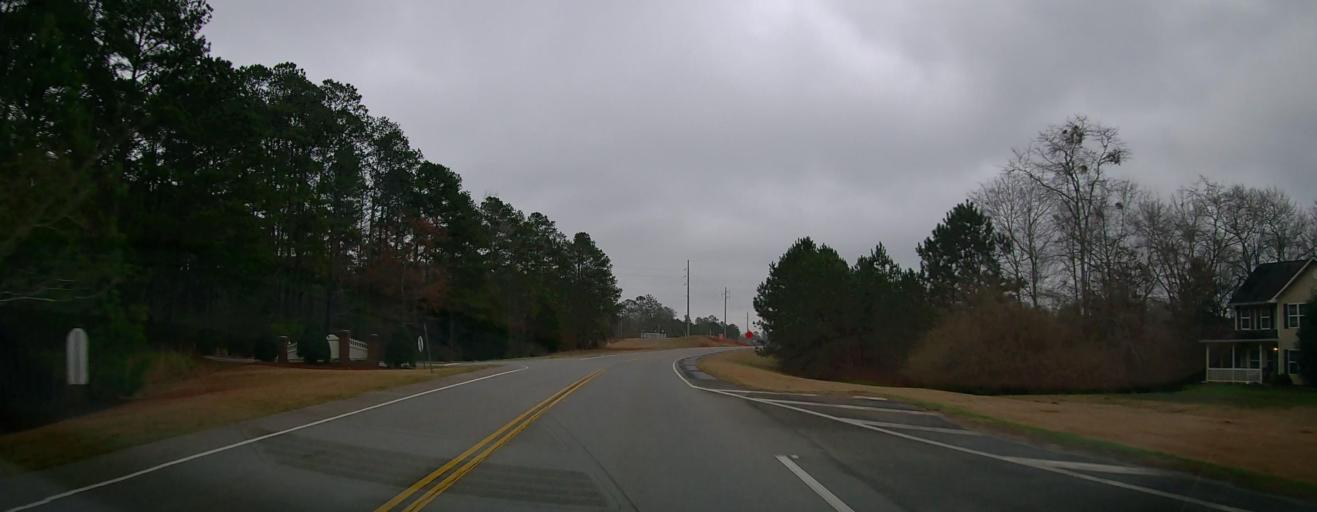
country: US
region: Georgia
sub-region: Lamar County
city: Barnesville
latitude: 33.0539
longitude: -84.1317
